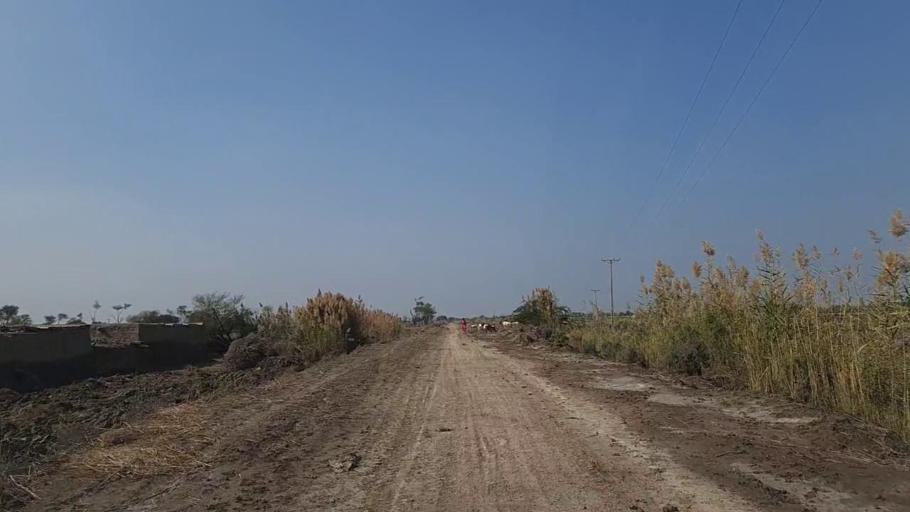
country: PK
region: Sindh
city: Nawabshah
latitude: 26.2901
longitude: 68.4874
